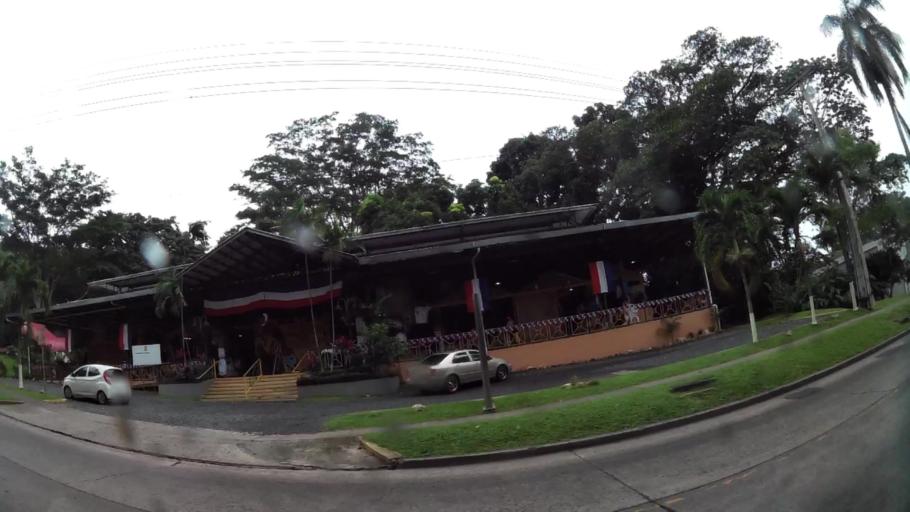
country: PA
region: Panama
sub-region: Distrito de Panama
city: Ancon
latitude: 8.9516
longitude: -79.5518
